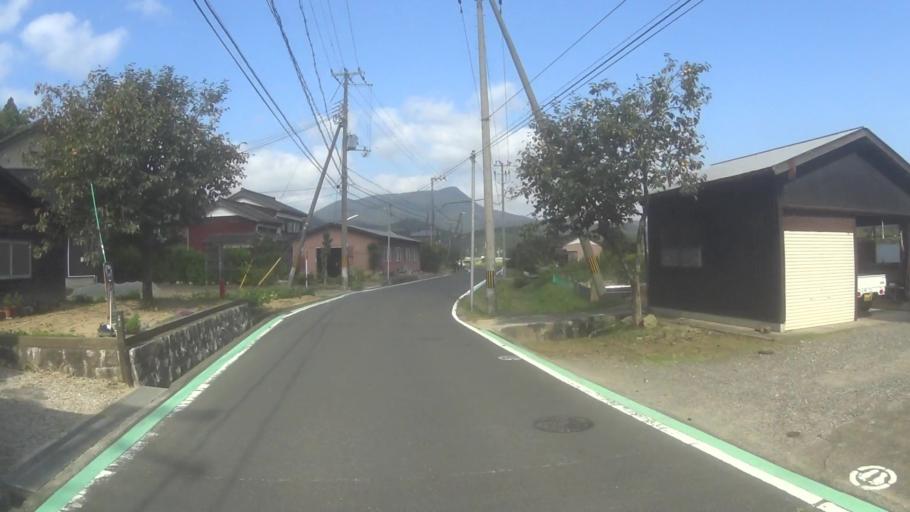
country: JP
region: Kyoto
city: Miyazu
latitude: 35.7116
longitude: 135.1024
